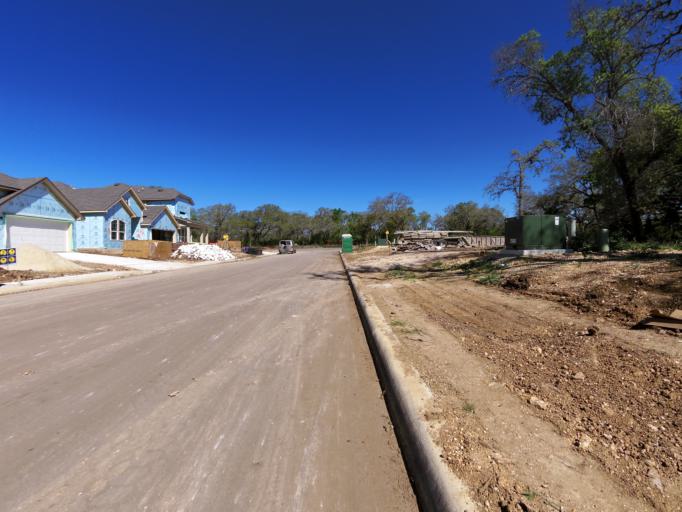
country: US
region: Texas
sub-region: Bexar County
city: Cross Mountain
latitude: 29.6837
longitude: -98.6449
